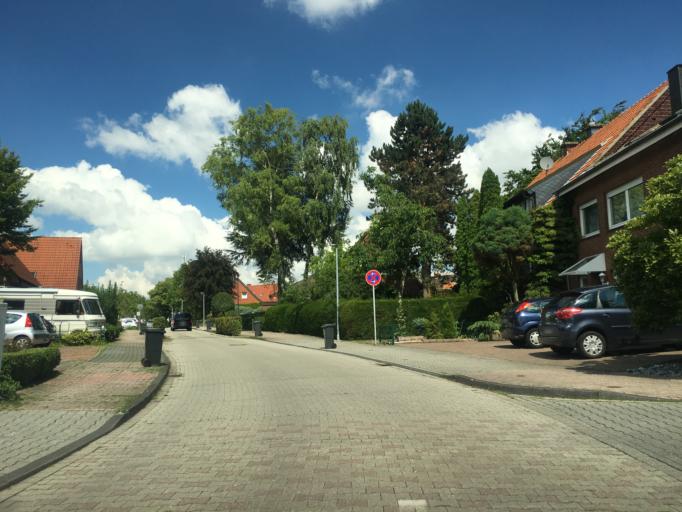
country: DE
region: North Rhine-Westphalia
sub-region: Regierungsbezirk Munster
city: Altenberge
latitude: 52.0450
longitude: 7.4723
